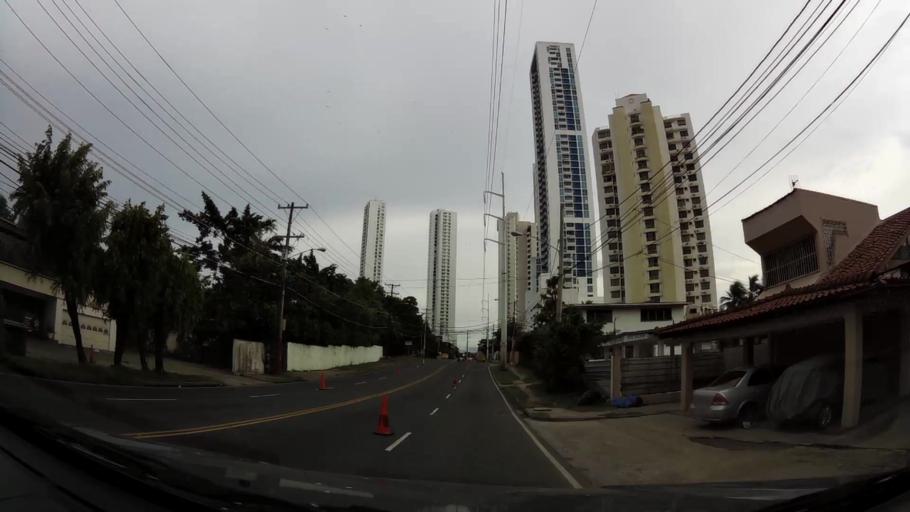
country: PA
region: Panama
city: Panama
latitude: 9.0009
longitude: -79.4967
